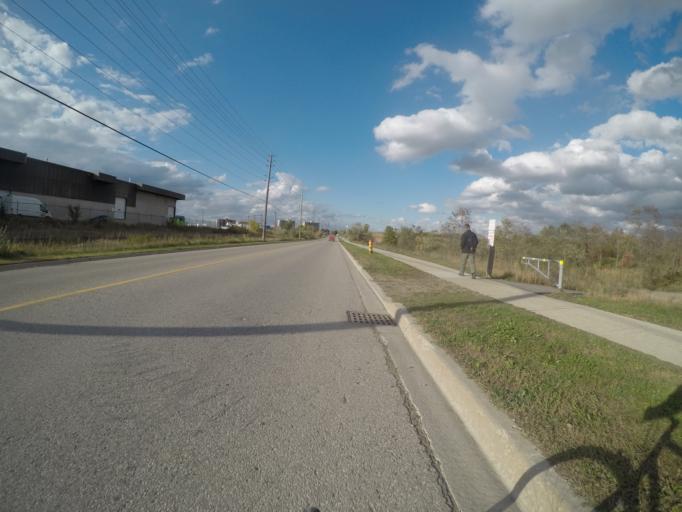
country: CA
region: Ontario
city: Kitchener
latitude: 43.4174
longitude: -80.4340
